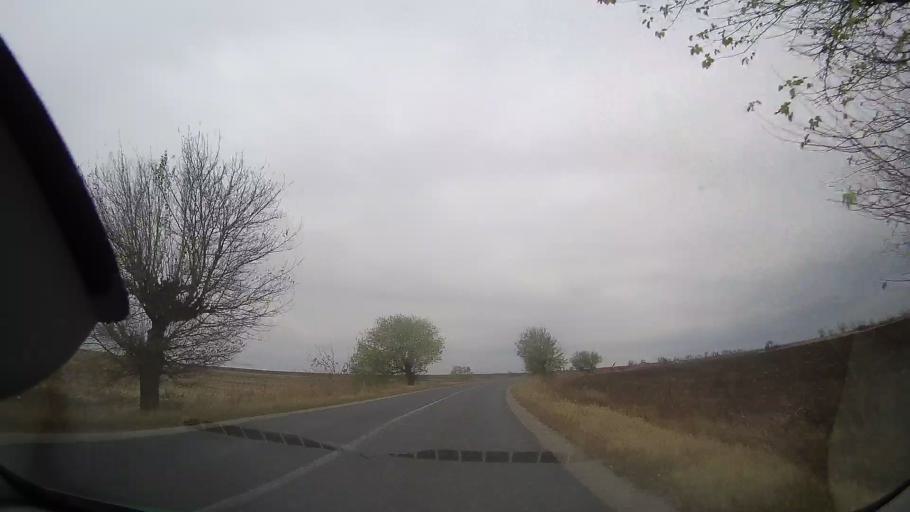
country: RO
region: Buzau
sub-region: Comuna Padina
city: Padina
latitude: 44.7785
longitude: 27.1560
